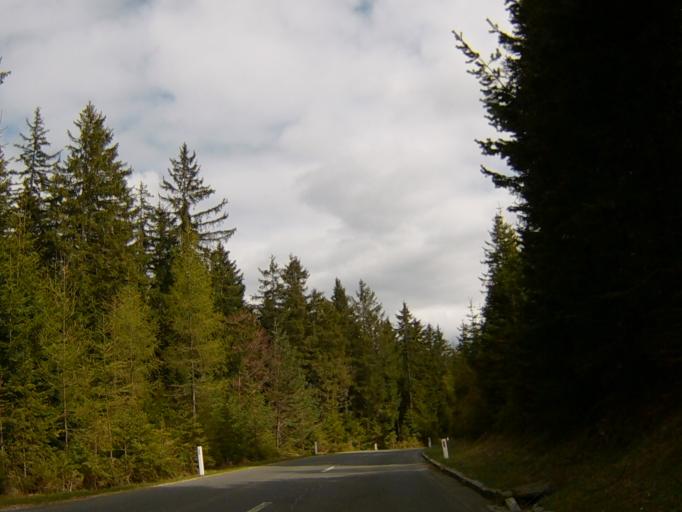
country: AT
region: Carinthia
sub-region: Politischer Bezirk Villach Land
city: Arnoldstein
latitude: 46.5935
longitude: 13.7500
